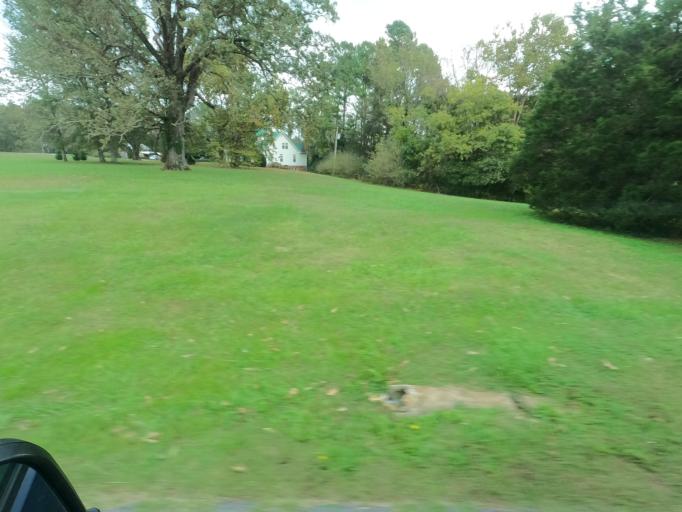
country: US
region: Tennessee
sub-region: Cheatham County
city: Kingston Springs
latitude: 36.1026
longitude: -87.0845
